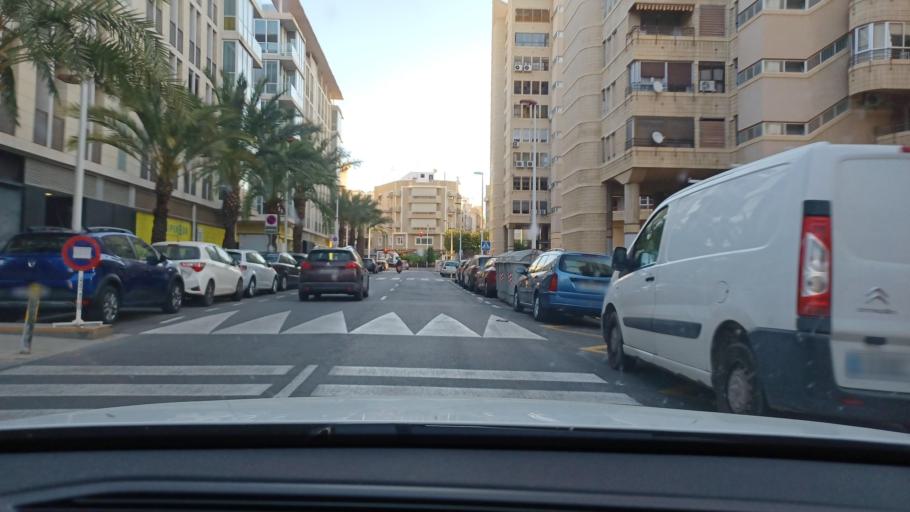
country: ES
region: Valencia
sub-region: Provincia de Alicante
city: Elche
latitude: 38.2632
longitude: -0.6946
